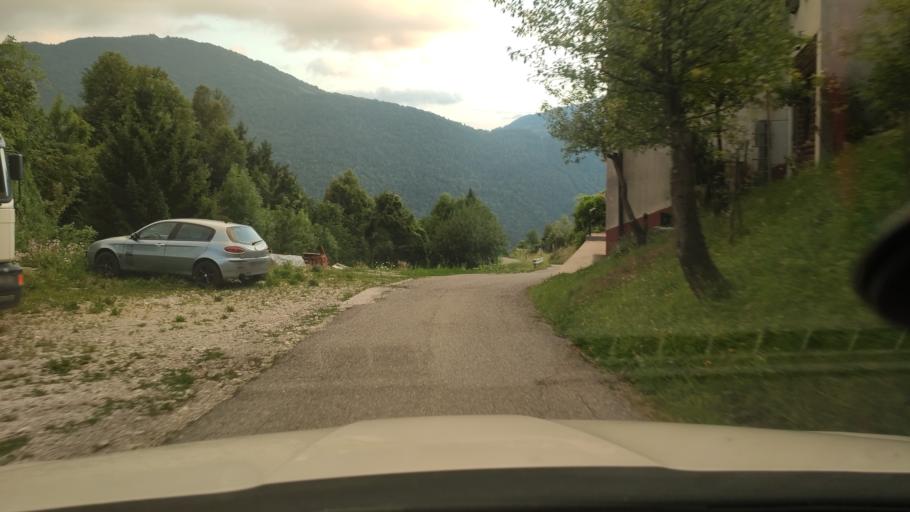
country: IT
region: Friuli Venezia Giulia
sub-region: Provincia di Udine
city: Cras
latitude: 46.2244
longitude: 13.6427
